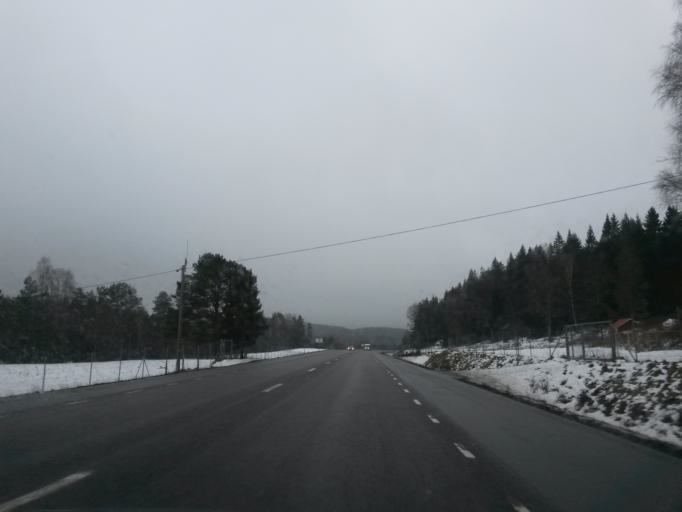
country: SE
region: Vaestra Goetaland
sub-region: Boras Kommun
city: Viskafors
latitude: 57.5809
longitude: 12.8593
